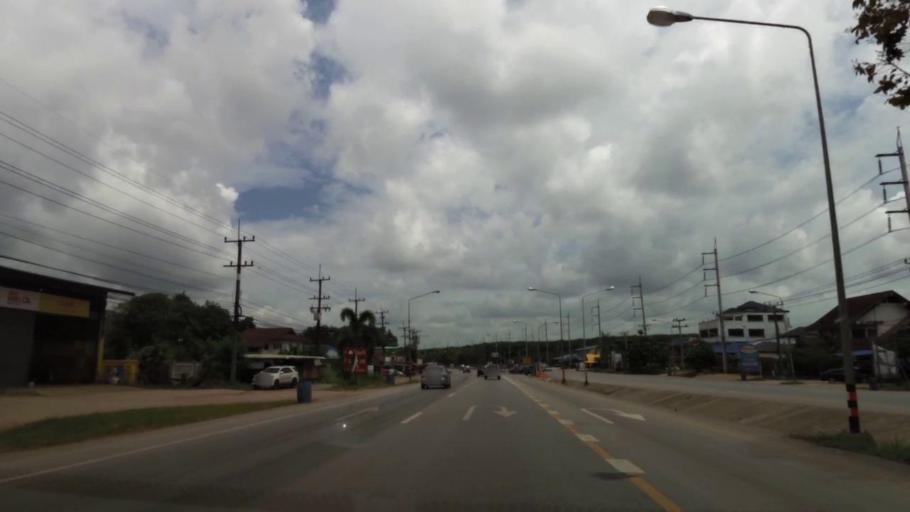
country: TH
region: Chanthaburi
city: Na Yai Am
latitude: 12.7867
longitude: 101.7903
